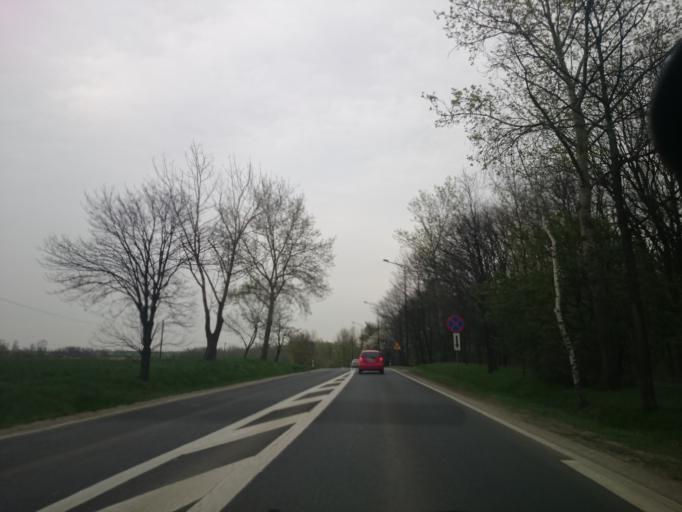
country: PL
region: Opole Voivodeship
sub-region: Powiat nyski
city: Nysa
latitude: 50.4784
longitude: 17.2812
